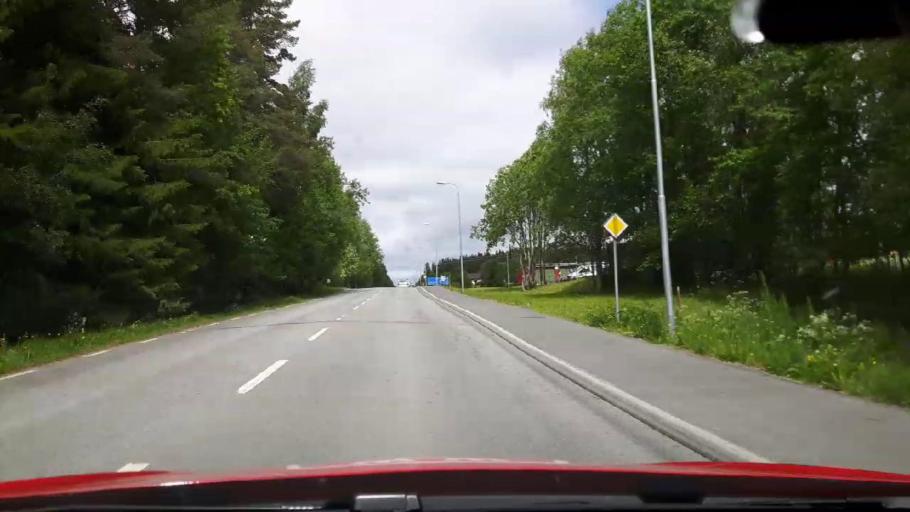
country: SE
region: Jaemtland
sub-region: Krokoms Kommun
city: Krokom
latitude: 63.3328
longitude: 14.4457
